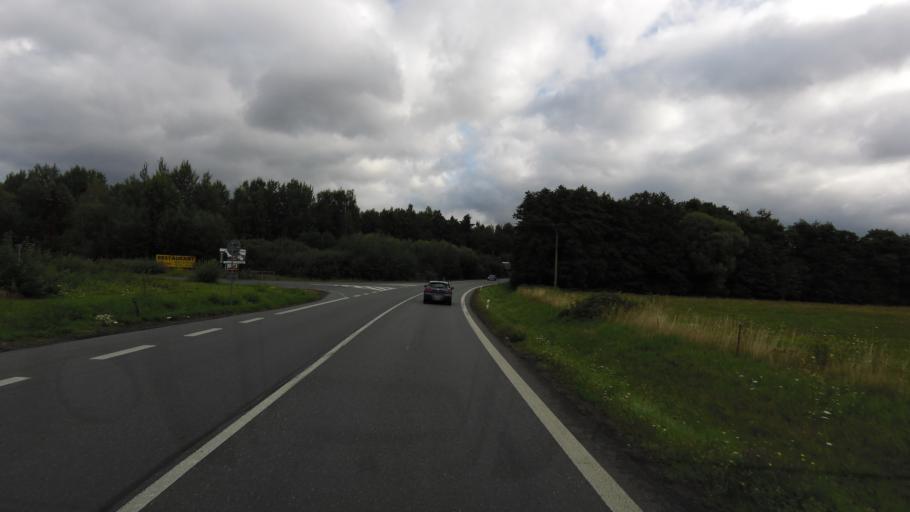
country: CZ
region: Plzensky
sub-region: Okres Domazlice
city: Domazlice
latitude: 49.4192
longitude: 12.8747
